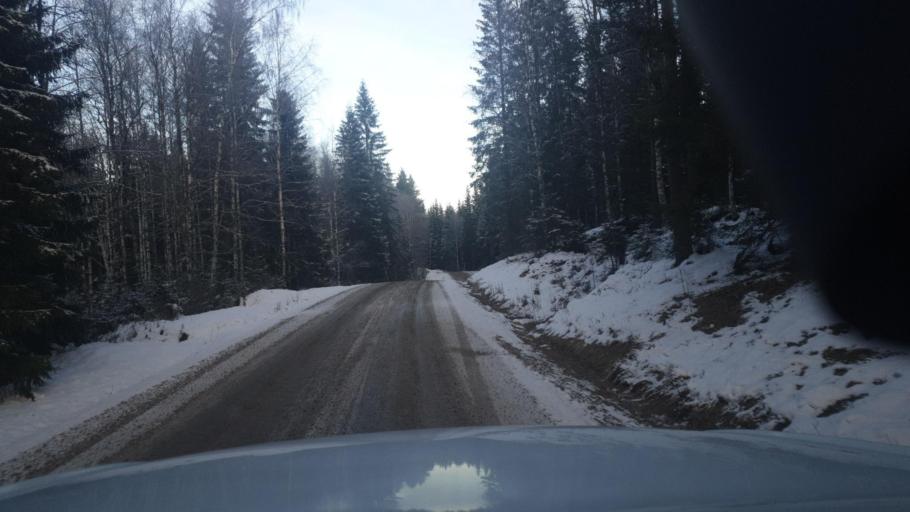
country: SE
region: Vaermland
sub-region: Arvika Kommun
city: Arvika
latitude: 59.9923
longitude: 12.6615
